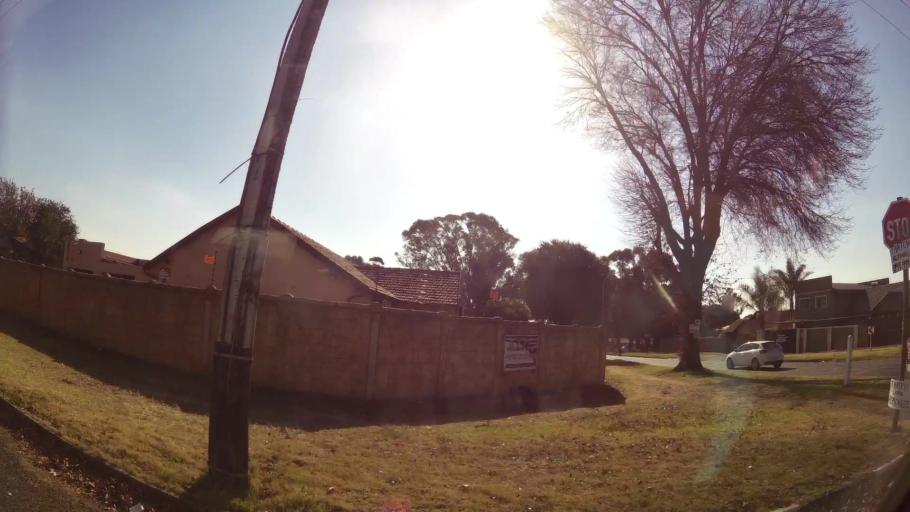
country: ZA
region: Gauteng
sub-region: City of Johannesburg Metropolitan Municipality
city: Johannesburg
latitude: -26.2541
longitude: 27.9964
